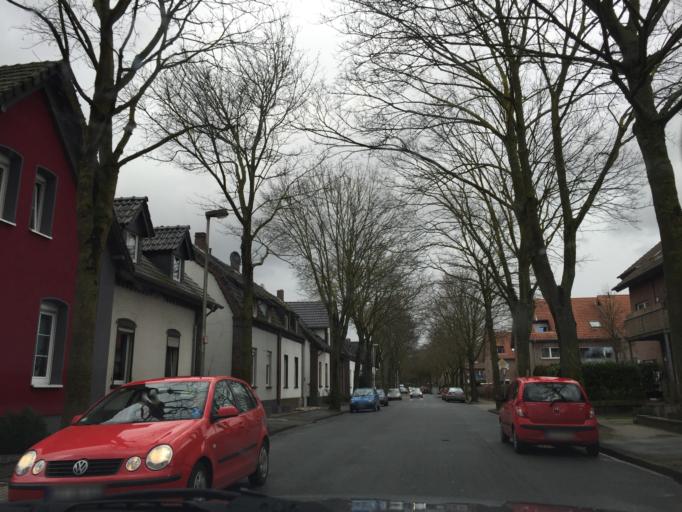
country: DE
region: North Rhine-Westphalia
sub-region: Regierungsbezirk Dusseldorf
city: Kleve
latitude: 51.7942
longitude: 6.1604
